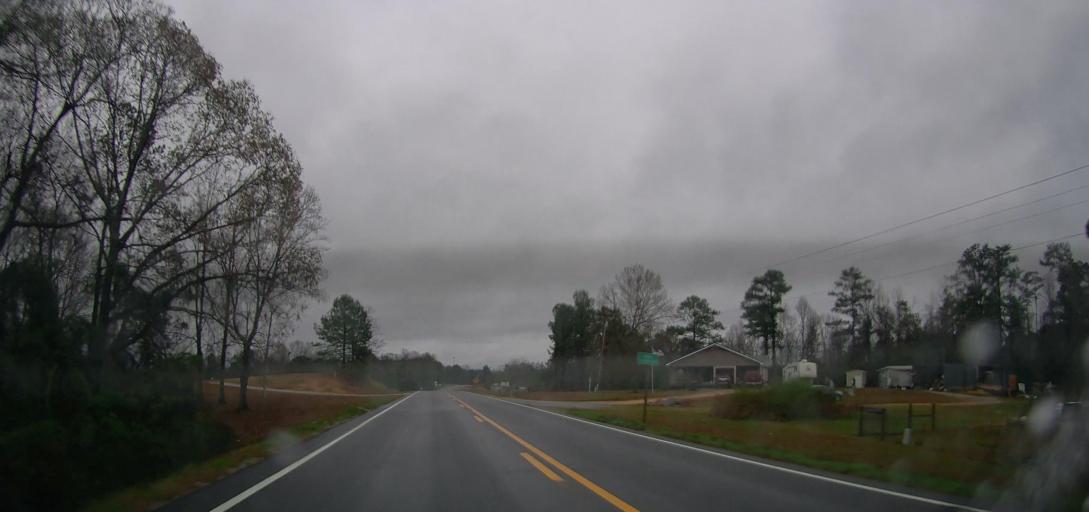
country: US
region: Alabama
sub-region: Chilton County
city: Thorsby
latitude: 32.8022
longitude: -86.9155
